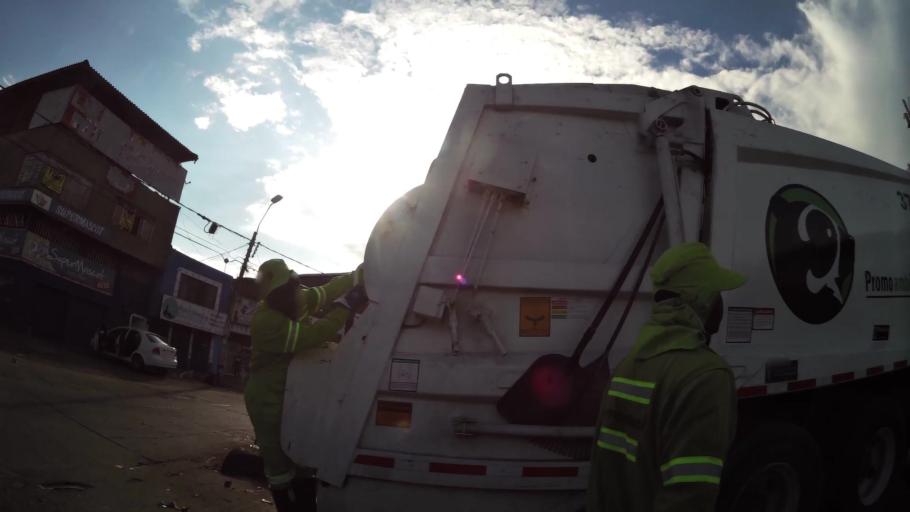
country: CO
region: Valle del Cauca
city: Cali
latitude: 3.4293
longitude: -76.5224
